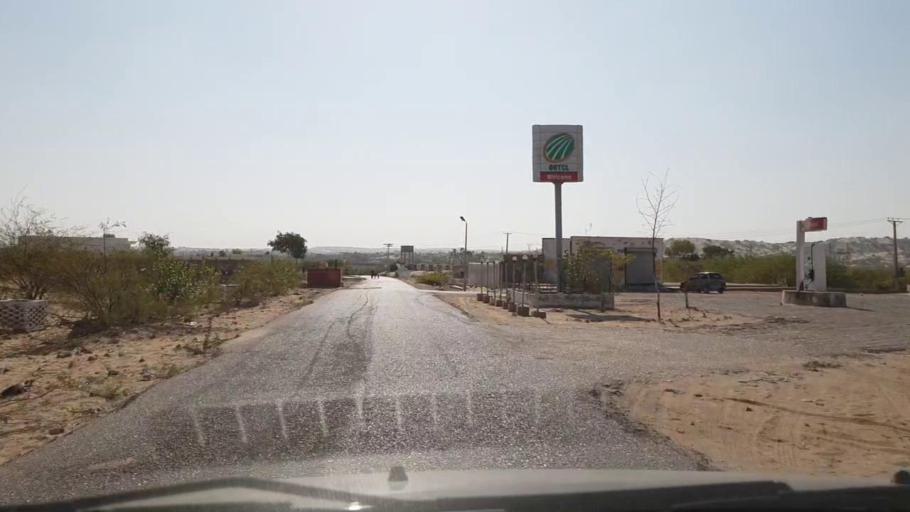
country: PK
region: Sindh
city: Diplo
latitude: 24.4803
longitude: 69.5813
